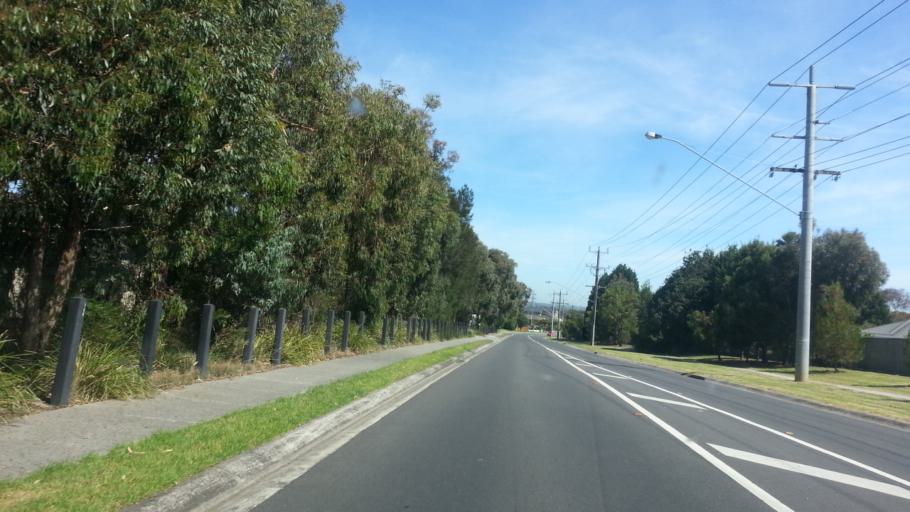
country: AU
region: Victoria
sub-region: Knox
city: Rowville
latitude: -37.9351
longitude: 145.2375
